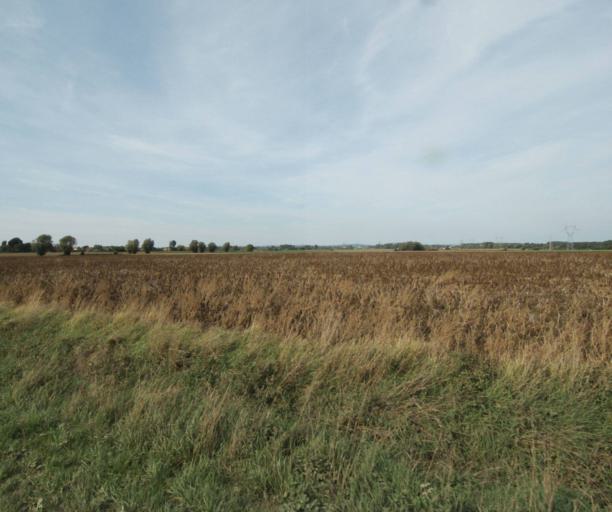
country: FR
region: Nord-Pas-de-Calais
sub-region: Departement du Nord
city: Radinghem-en-Weppes
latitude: 50.6175
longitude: 2.9184
